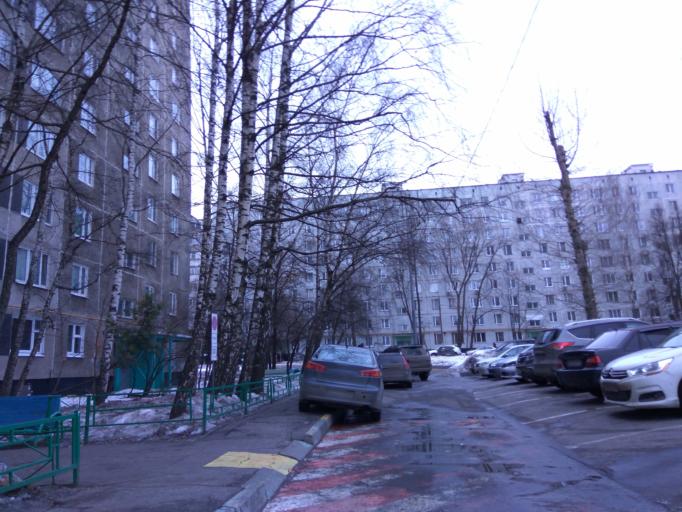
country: RU
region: Moscow
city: Biryulevo
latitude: 55.5951
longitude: 37.6655
